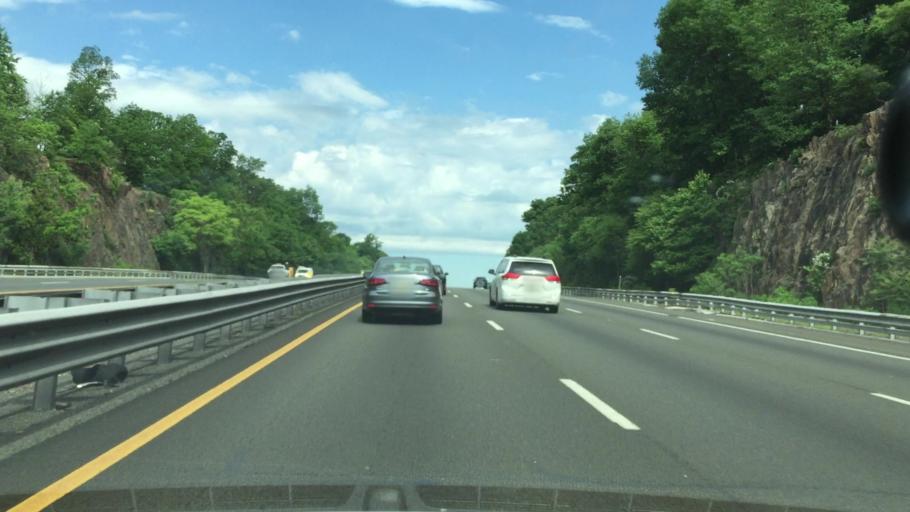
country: US
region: New Jersey
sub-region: Essex County
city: West Orange
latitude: 40.8006
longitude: -74.2648
